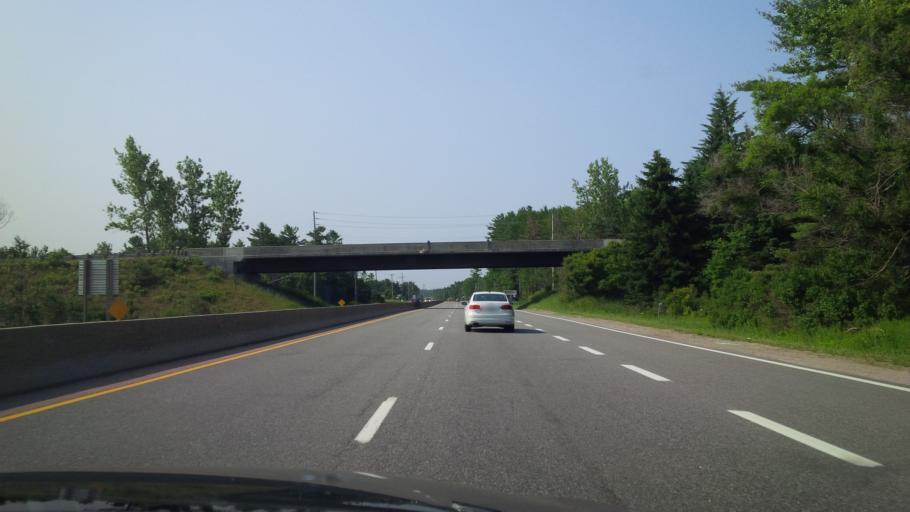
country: CA
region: Ontario
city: Gravenhurst
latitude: 44.8440
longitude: -79.3175
